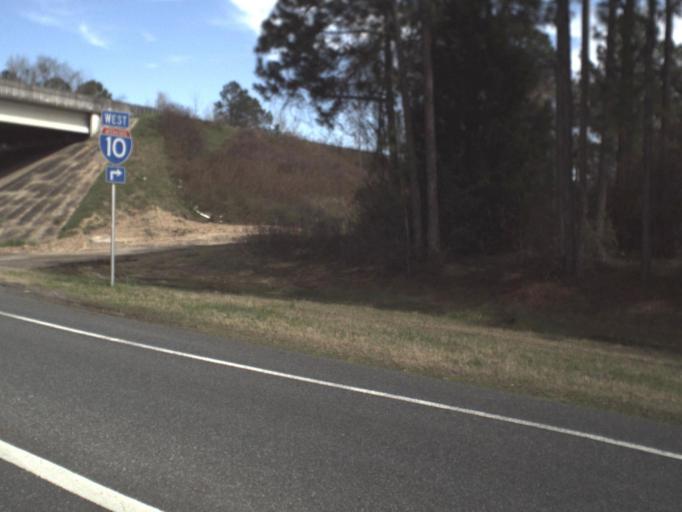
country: US
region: Florida
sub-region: Jackson County
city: Marianna
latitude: 30.7524
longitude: -85.3821
